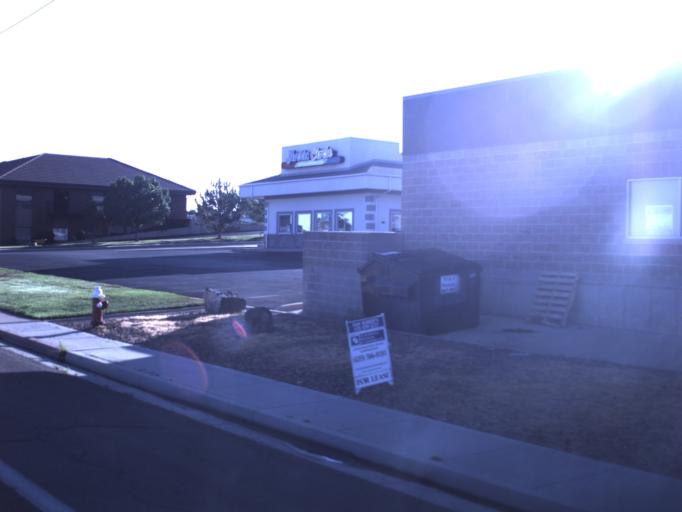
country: US
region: Utah
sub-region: Iron County
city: Cedar City
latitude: 37.7103
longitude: -113.0615
